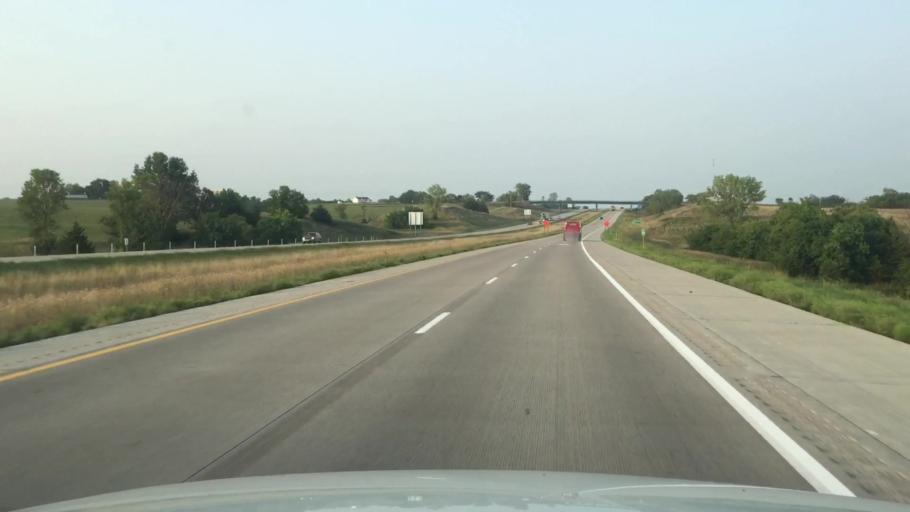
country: US
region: Iowa
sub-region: Decatur County
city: Lamoni
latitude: 40.6328
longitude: -93.8812
